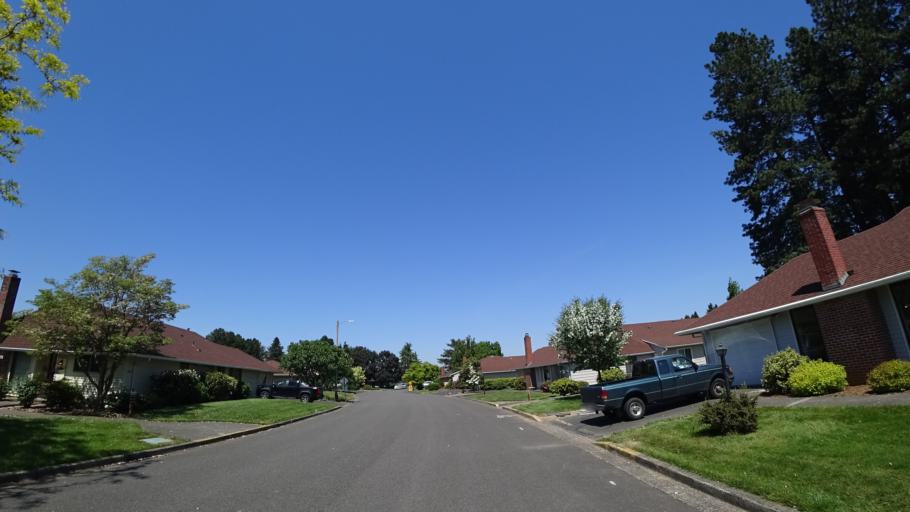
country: US
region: Oregon
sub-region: Washington County
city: Beaverton
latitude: 45.4827
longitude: -122.8244
